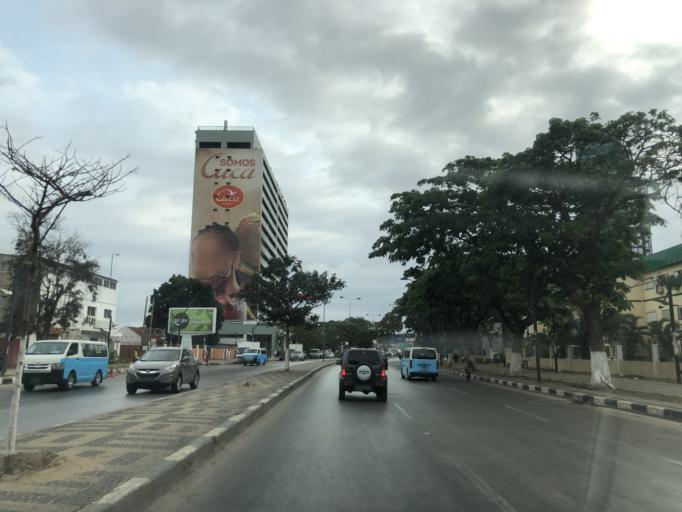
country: AO
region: Luanda
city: Luanda
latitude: -8.8362
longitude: 13.2376
